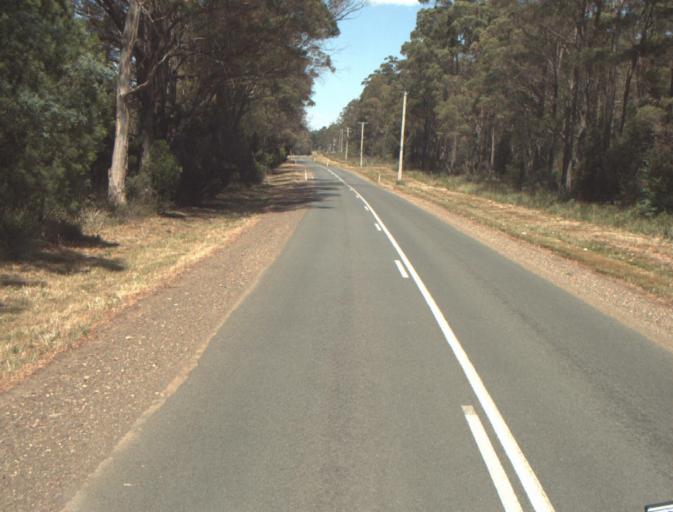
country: AU
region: Tasmania
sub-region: Launceston
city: Mayfield
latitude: -41.2850
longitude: 147.1265
